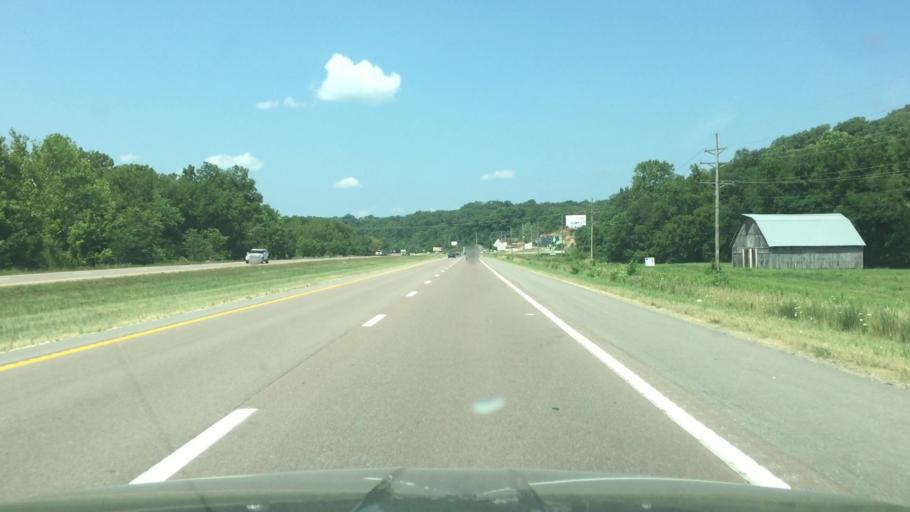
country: US
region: Missouri
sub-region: Miller County
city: Lake Ozark
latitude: 38.2441
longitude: -92.6052
